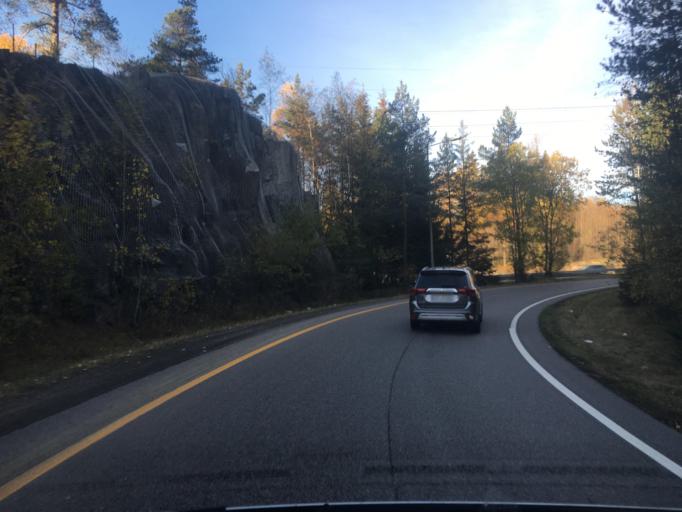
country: NO
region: Akershus
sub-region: Lorenskog
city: Kjenn
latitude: 59.9474
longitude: 10.9455
